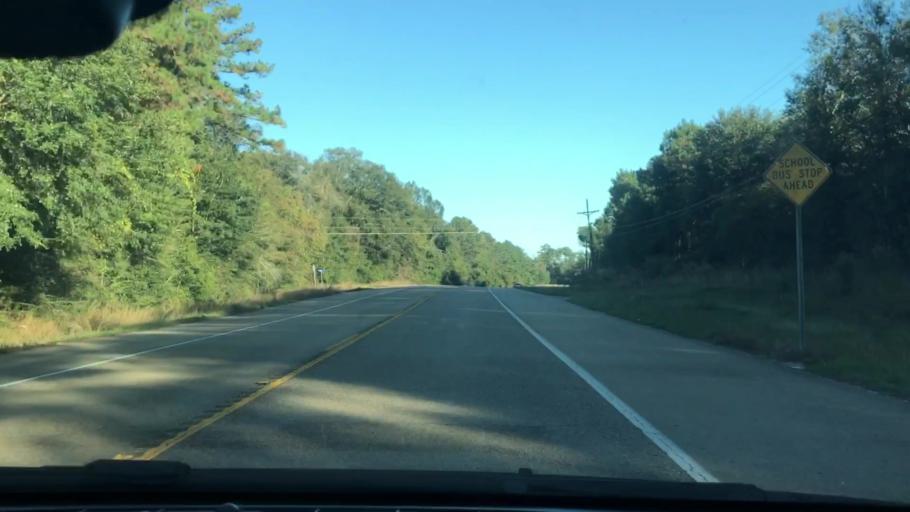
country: US
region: Louisiana
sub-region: Washington Parish
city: Bogalusa
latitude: 30.6087
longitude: -89.8826
